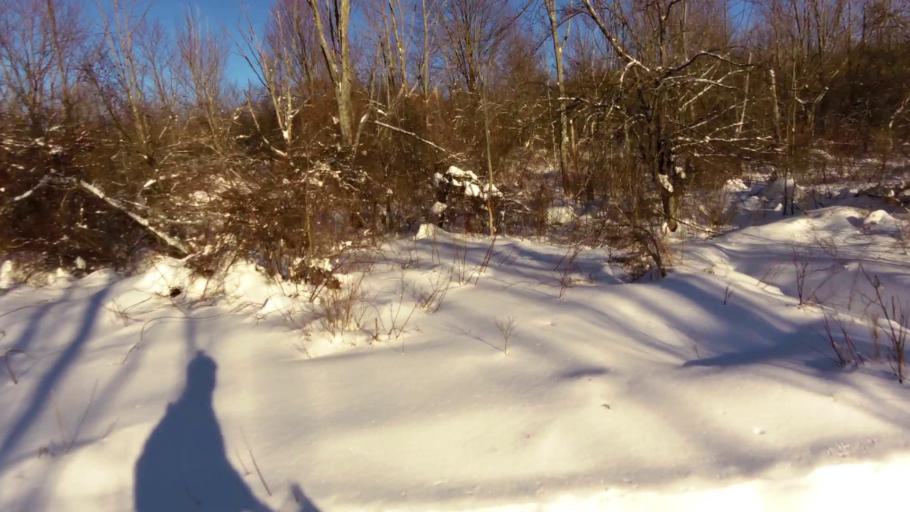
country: US
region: New York
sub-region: Chautauqua County
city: Mayville
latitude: 42.2476
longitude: -79.3919
